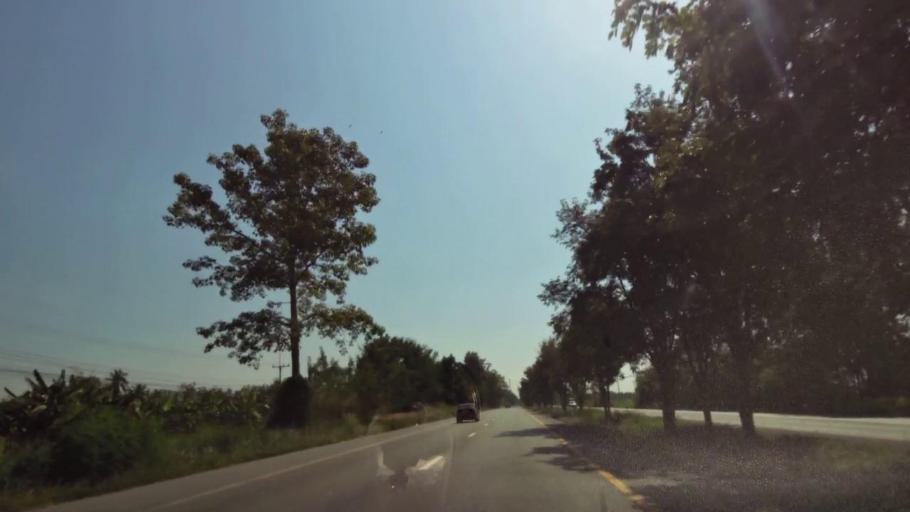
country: TH
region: Nakhon Sawan
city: Kao Liao
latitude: 15.8829
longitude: 100.1154
